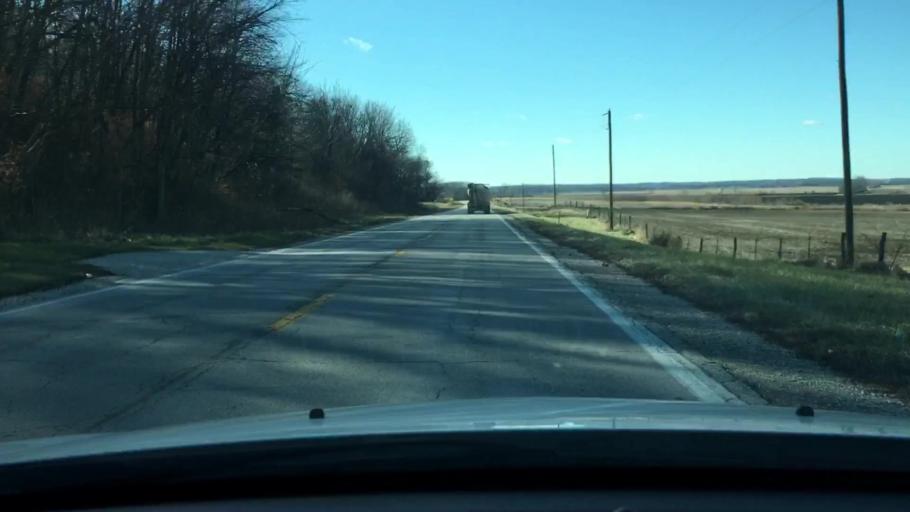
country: US
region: Illinois
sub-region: Morgan County
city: Meredosia
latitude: 39.7433
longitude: -90.5455
